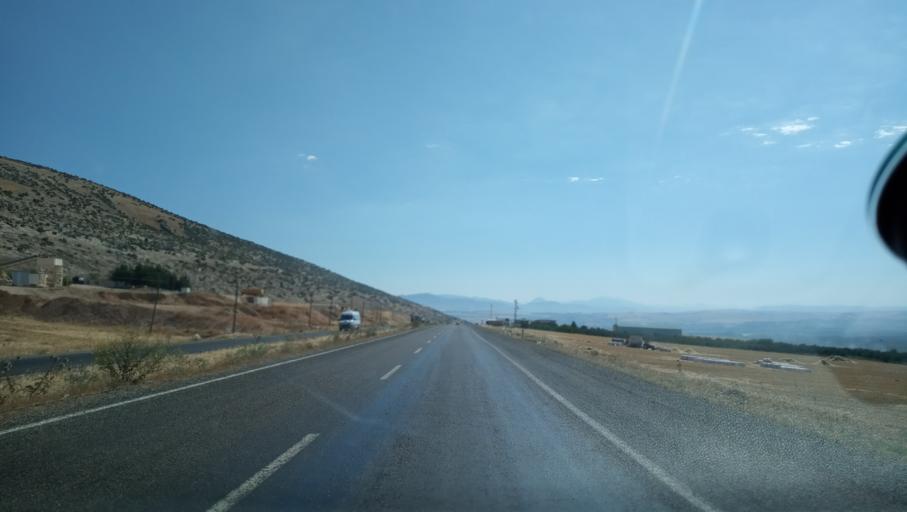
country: TR
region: Diyarbakir
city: Malabadi
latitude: 38.1228
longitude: 41.1558
